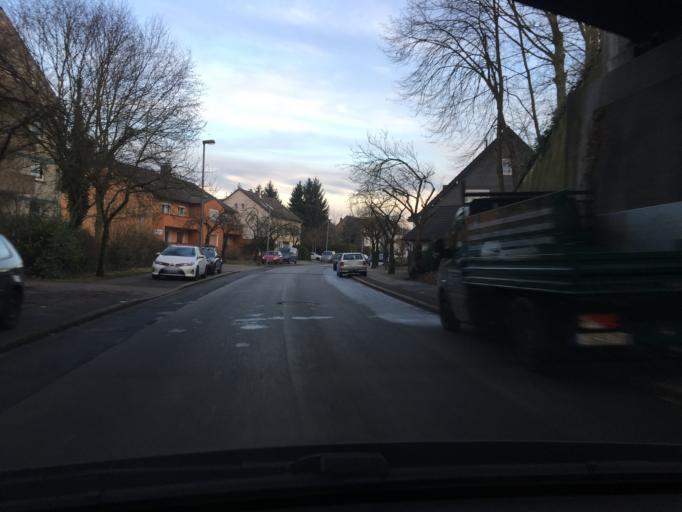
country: DE
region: North Rhine-Westphalia
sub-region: Regierungsbezirk Dusseldorf
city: Oberhausen
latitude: 51.4535
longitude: 6.8357
